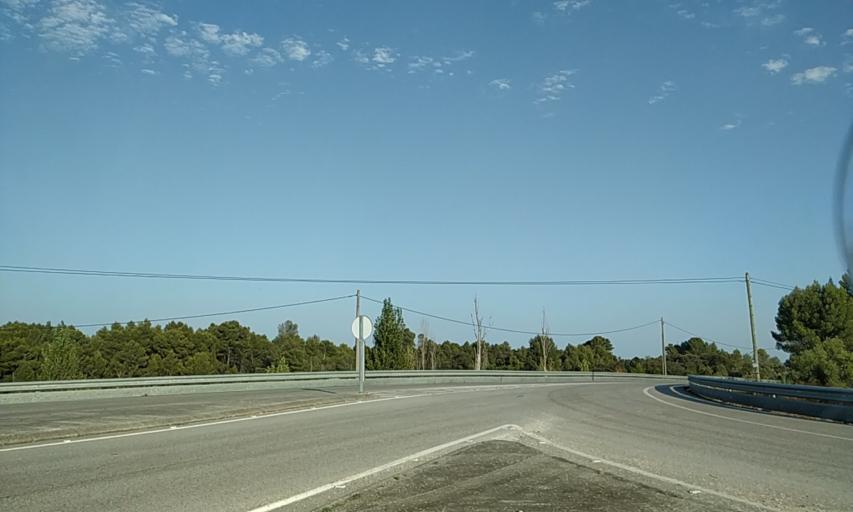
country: PT
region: Santarem
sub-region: Alcanena
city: Alcanena
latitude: 39.4355
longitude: -8.6266
